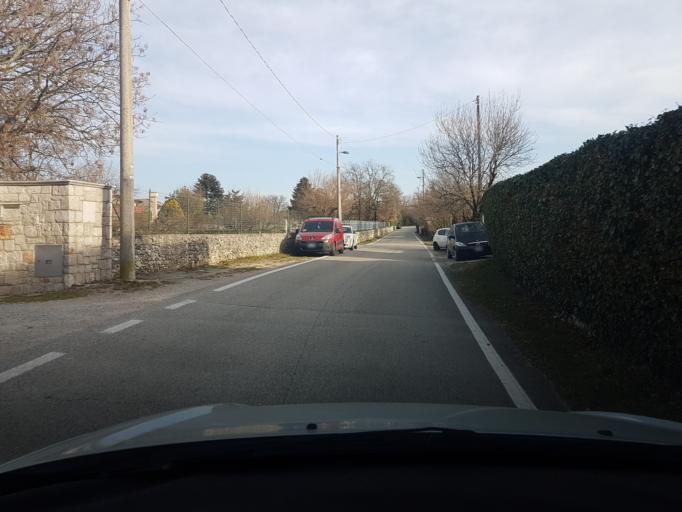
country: IT
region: Friuli Venezia Giulia
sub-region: Provincia di Trieste
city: Prosecco-Contovello
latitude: 45.7085
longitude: 13.7377
